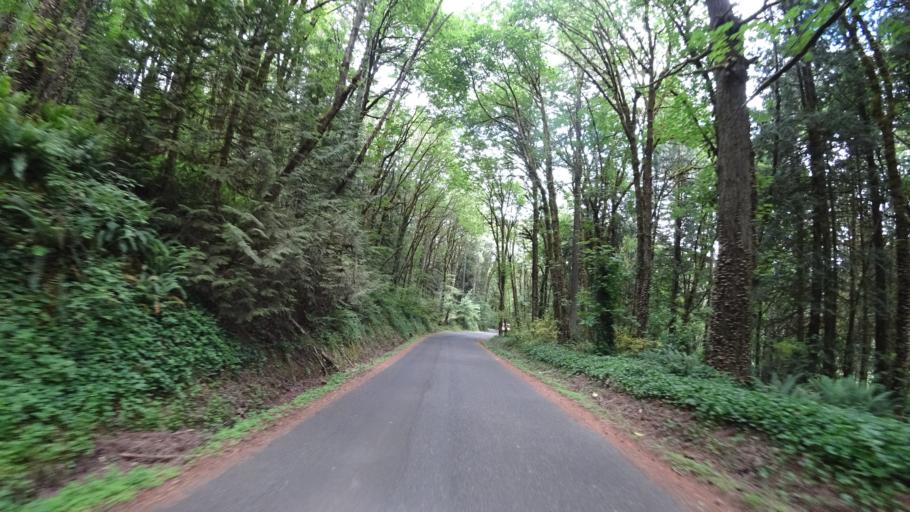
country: US
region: Oregon
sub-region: Clackamas County
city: Lake Oswego
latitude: 45.4517
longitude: -122.6915
